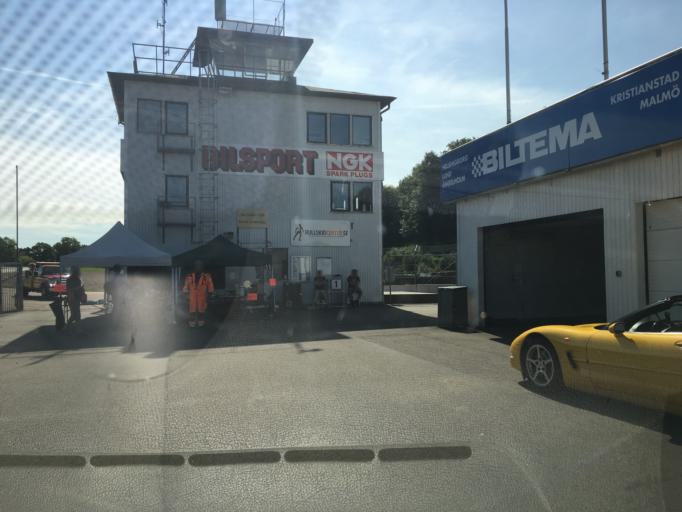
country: SE
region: Skane
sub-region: Svalovs Kommun
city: Kagerod
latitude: 55.9870
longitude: 13.1148
